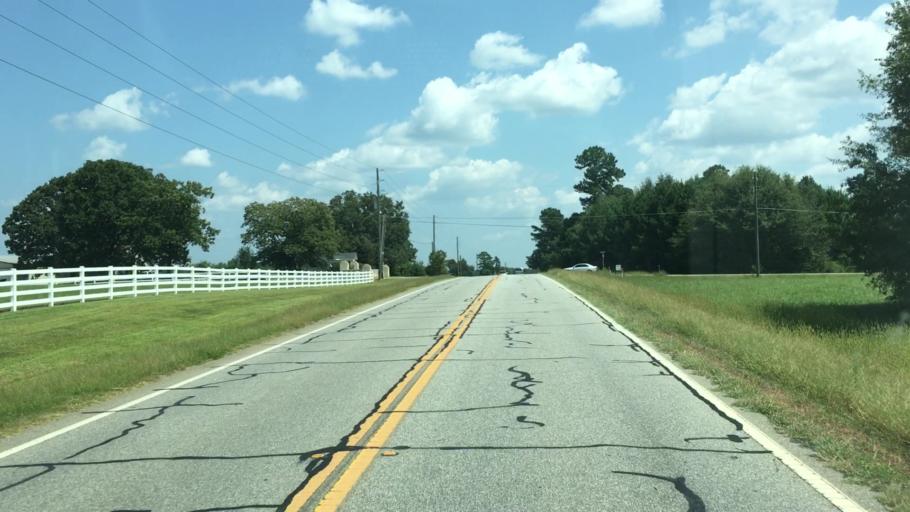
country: US
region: Georgia
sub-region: Barrow County
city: Statham
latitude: 33.9378
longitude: -83.6333
